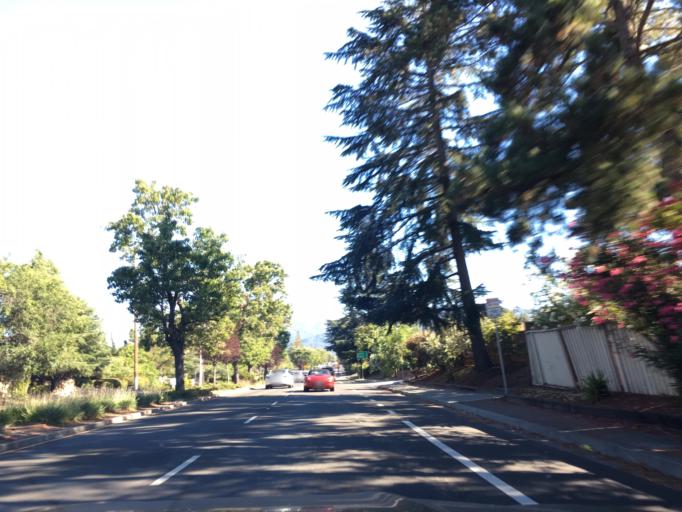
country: US
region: California
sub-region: Santa Clara County
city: Saratoga
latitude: 37.2872
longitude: -122.0326
